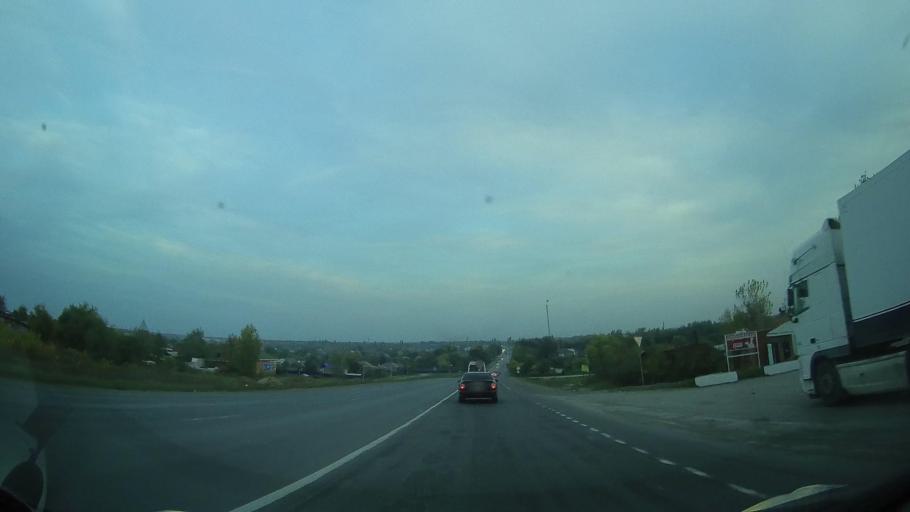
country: RU
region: Rostov
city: Kagal'nitskaya
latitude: 46.8871
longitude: 40.1416
